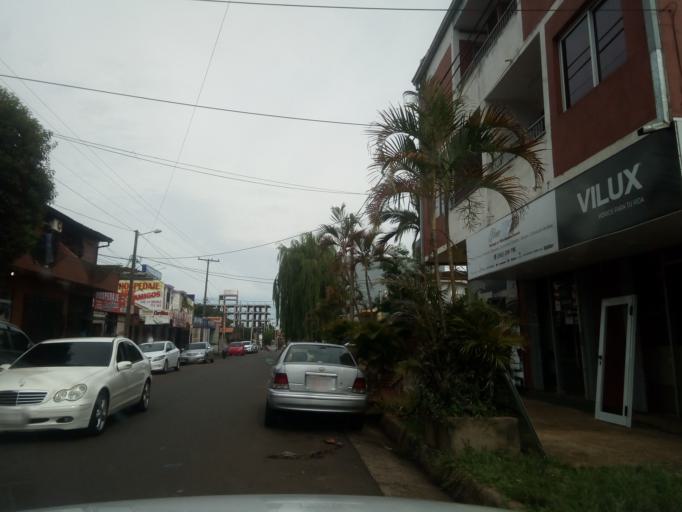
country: PY
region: Itapua
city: Encarnacion
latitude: -27.3569
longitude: -55.8552
